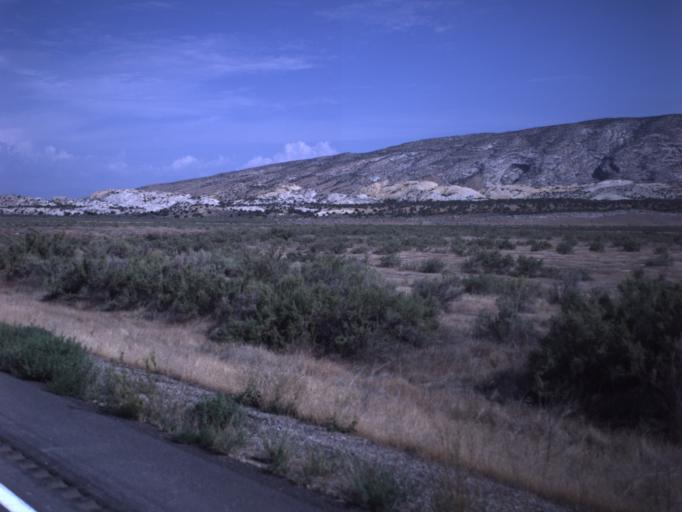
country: US
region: Utah
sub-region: Uintah County
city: Naples
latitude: 40.3110
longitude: -109.2217
